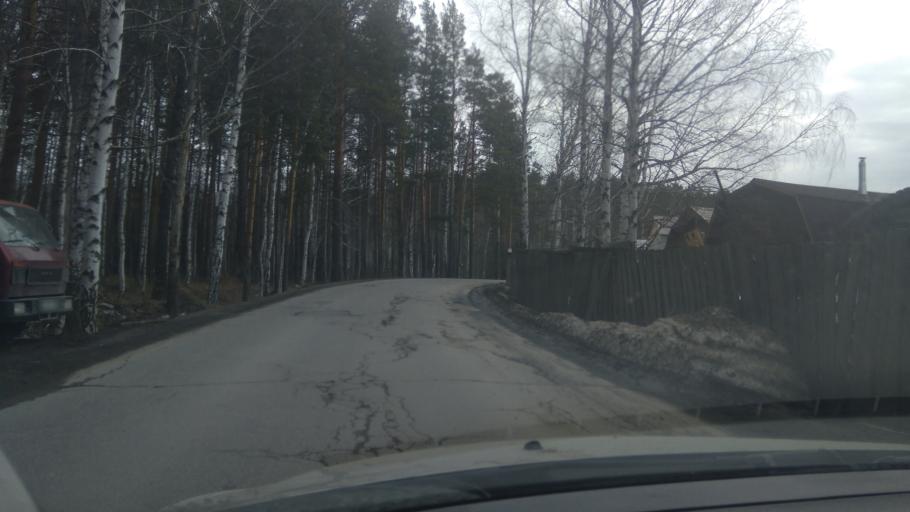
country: RU
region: Sverdlovsk
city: Severka
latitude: 56.8422
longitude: 60.3852
